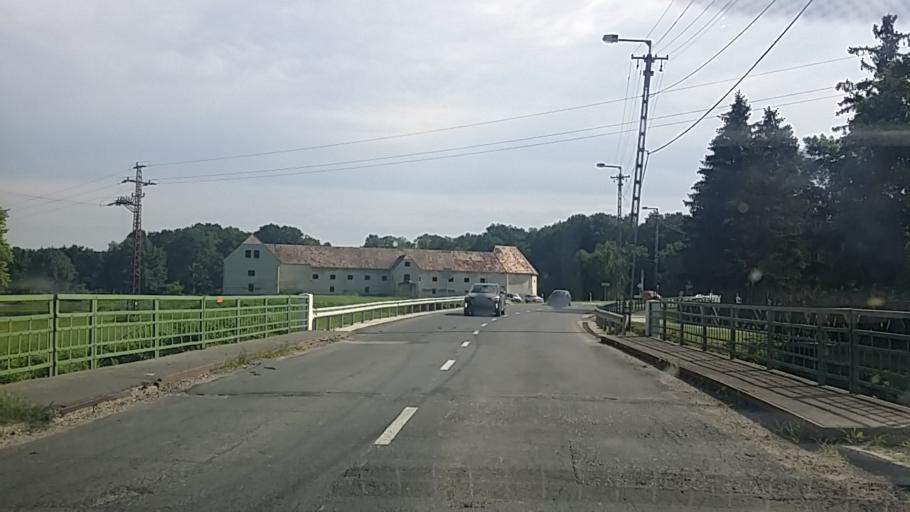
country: HU
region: Zala
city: Lenti
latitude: 46.6250
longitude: 16.5494
